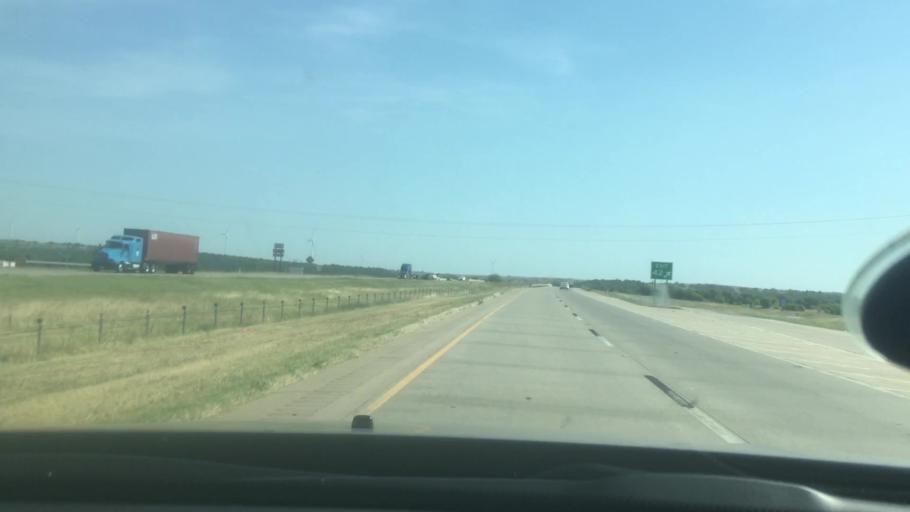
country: US
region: Oklahoma
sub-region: Carter County
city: Ardmore
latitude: 34.3296
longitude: -97.1535
